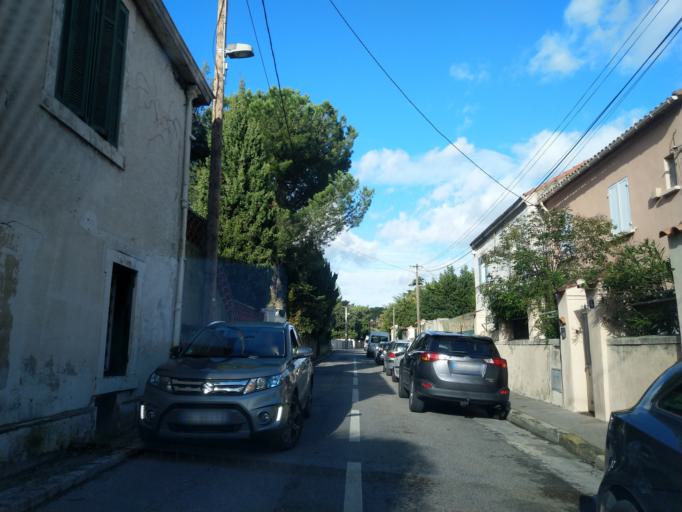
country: FR
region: Provence-Alpes-Cote d'Azur
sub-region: Departement des Bouches-du-Rhone
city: Marseille 12
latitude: 43.3089
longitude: 5.4363
